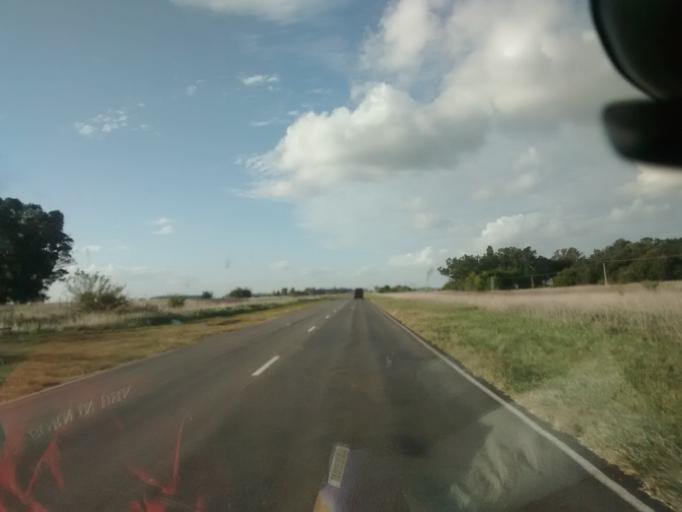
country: AR
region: Buenos Aires
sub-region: Partido de Ayacucho
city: Ayacucho
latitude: -36.6492
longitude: -58.5736
